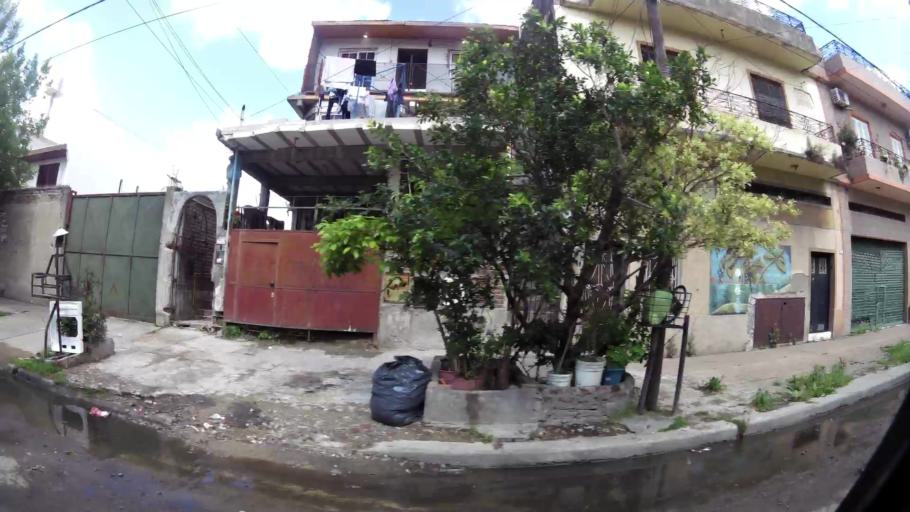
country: AR
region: Buenos Aires
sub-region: Partido de Lanus
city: Lanus
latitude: -34.6825
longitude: -58.4248
